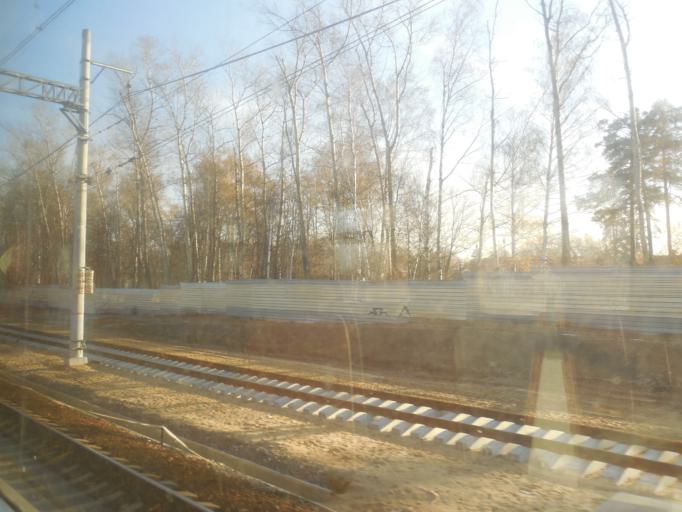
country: RU
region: Moskovskaya
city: Saltykovka
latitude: 55.7564
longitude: 37.9302
